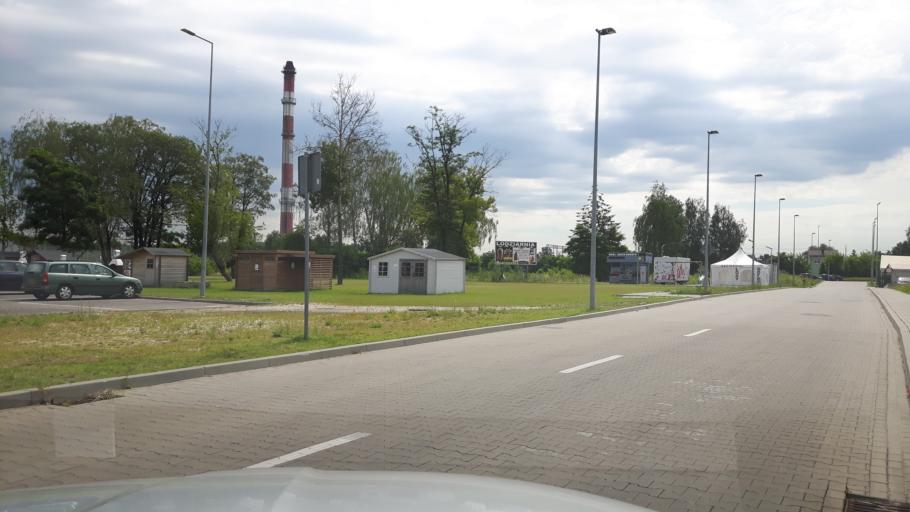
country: PL
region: Masovian Voivodeship
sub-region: Powiat wolominski
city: Nowe Lipiny
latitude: 52.3581
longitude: 21.2591
